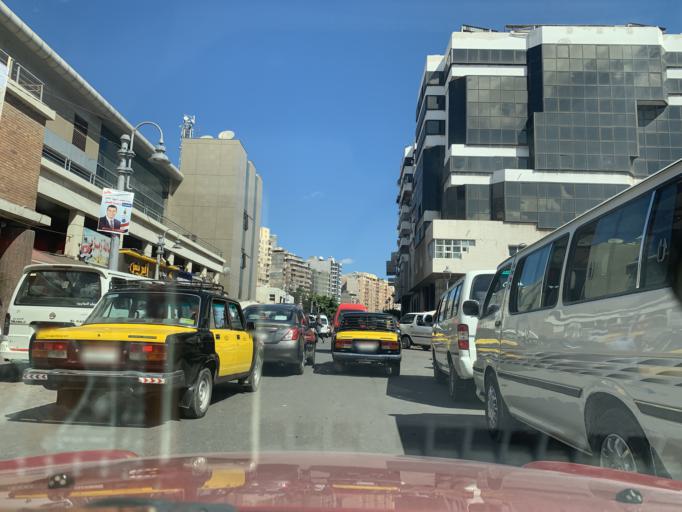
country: EG
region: Alexandria
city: Alexandria
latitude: 31.2191
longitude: 29.9434
